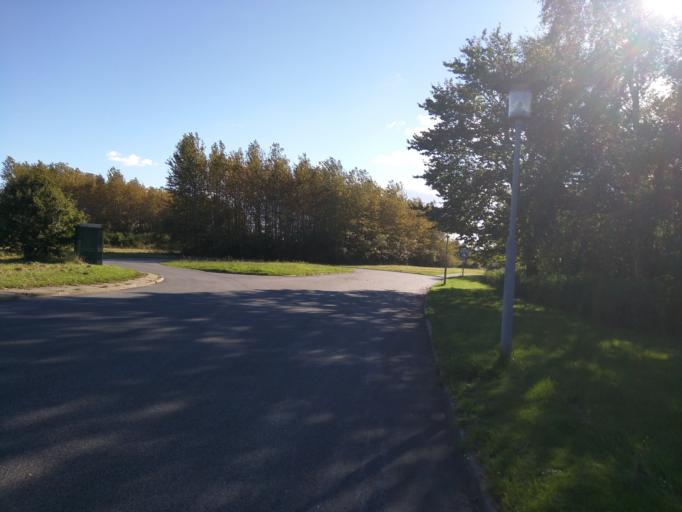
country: DK
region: Central Jutland
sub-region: Viborg Kommune
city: Viborg
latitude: 56.4380
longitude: 9.3856
